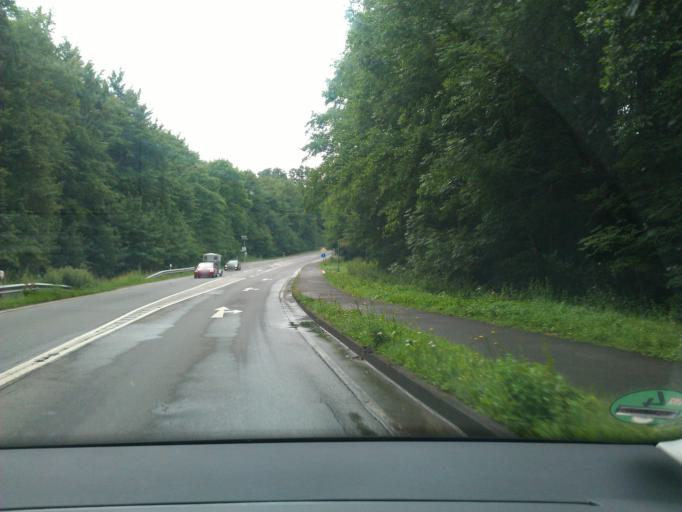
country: DE
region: North Rhine-Westphalia
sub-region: Regierungsbezirk Koln
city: Aachen
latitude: 50.7328
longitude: 6.1147
